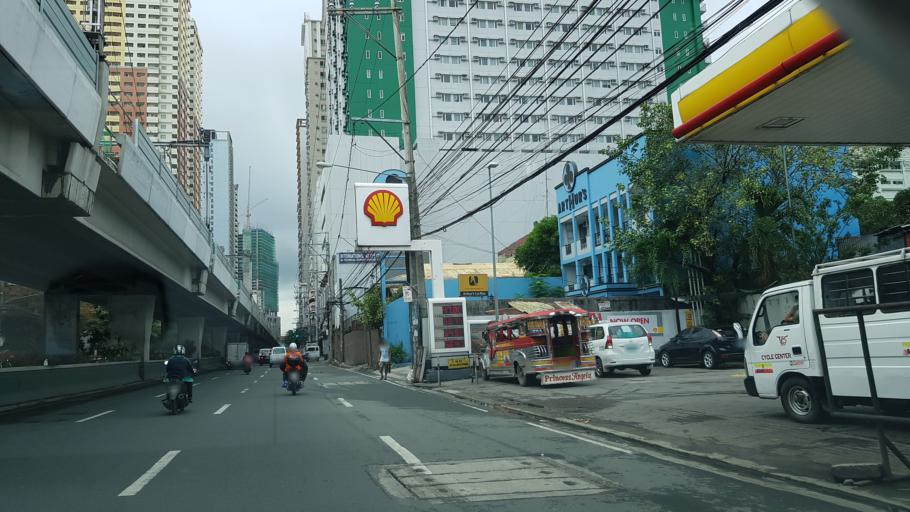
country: PH
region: Metro Manila
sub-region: City of Manila
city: Port Area
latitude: 14.5687
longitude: 120.9923
